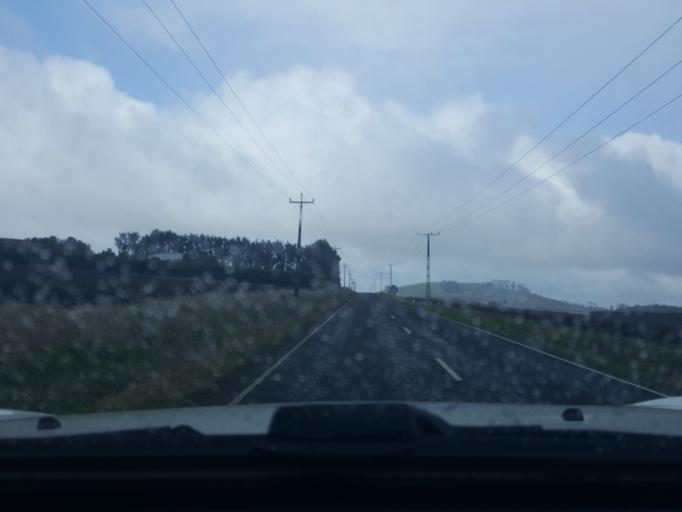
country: NZ
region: Auckland
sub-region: Auckland
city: Pukekohe East
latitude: -37.3120
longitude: 174.9872
